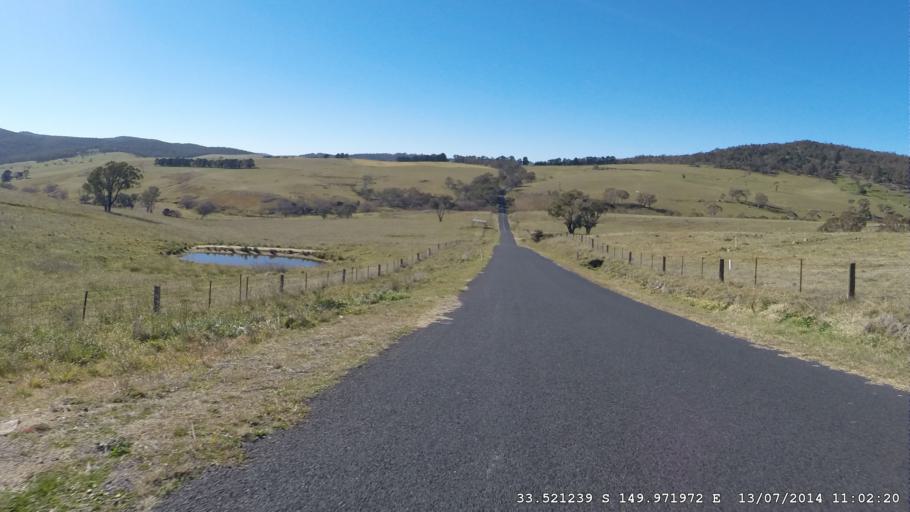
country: AU
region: New South Wales
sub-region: Lithgow
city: Bowenfels
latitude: -33.5211
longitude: 149.9719
